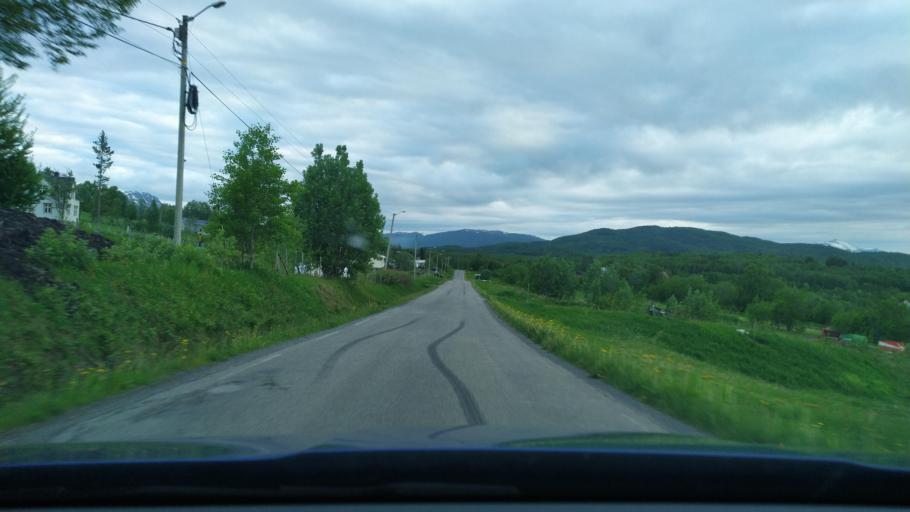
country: NO
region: Troms
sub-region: Tranoy
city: Vangsvika
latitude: 69.1138
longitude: 17.7925
